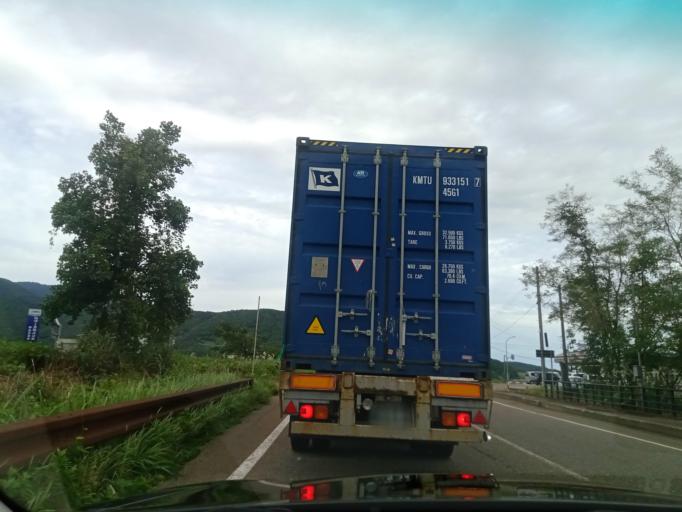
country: JP
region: Niigata
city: Arai
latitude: 37.0196
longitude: 138.2278
